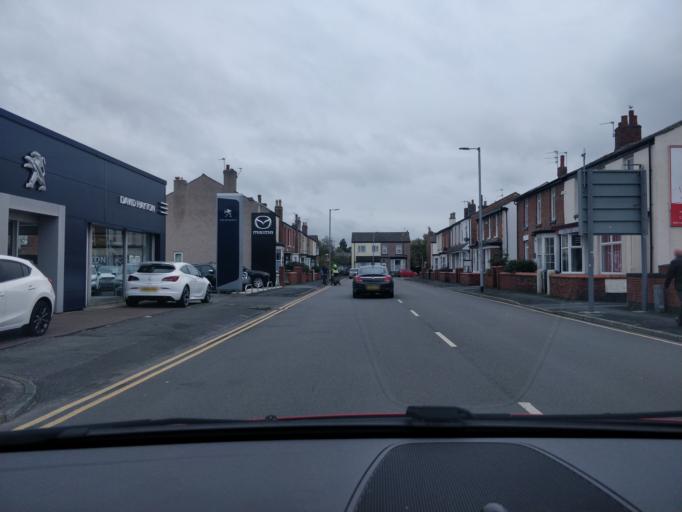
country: GB
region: England
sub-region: Sefton
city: Southport
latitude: 53.6446
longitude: -3.0020
